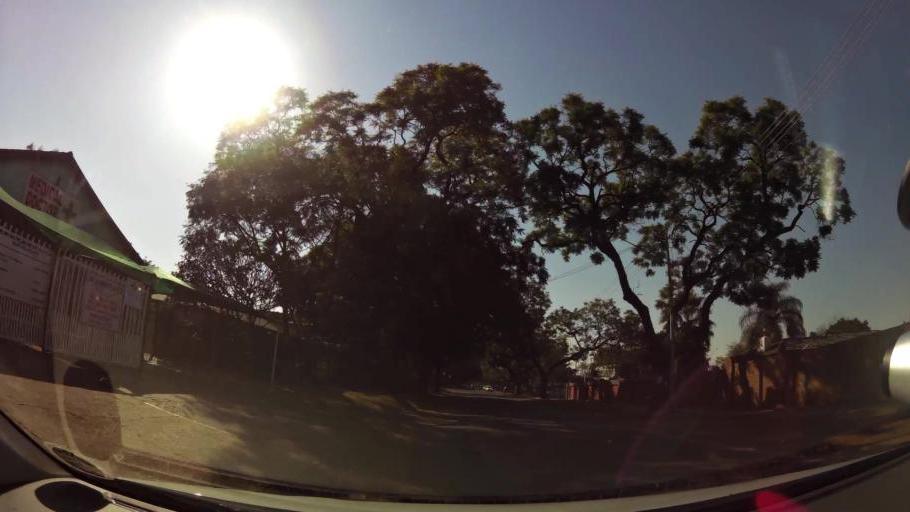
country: ZA
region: Gauteng
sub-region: City of Tshwane Metropolitan Municipality
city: Pretoria
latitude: -25.6783
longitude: 28.1722
